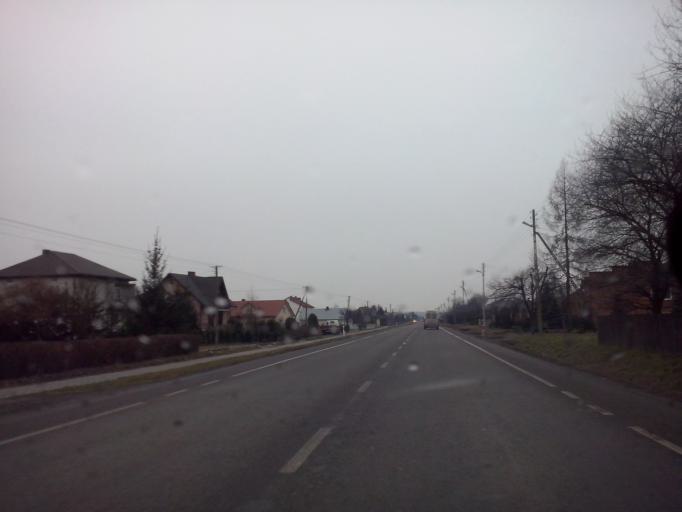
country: PL
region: Lublin Voivodeship
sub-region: Powiat zamojski
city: Michalow
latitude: 50.7179
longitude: 23.0481
